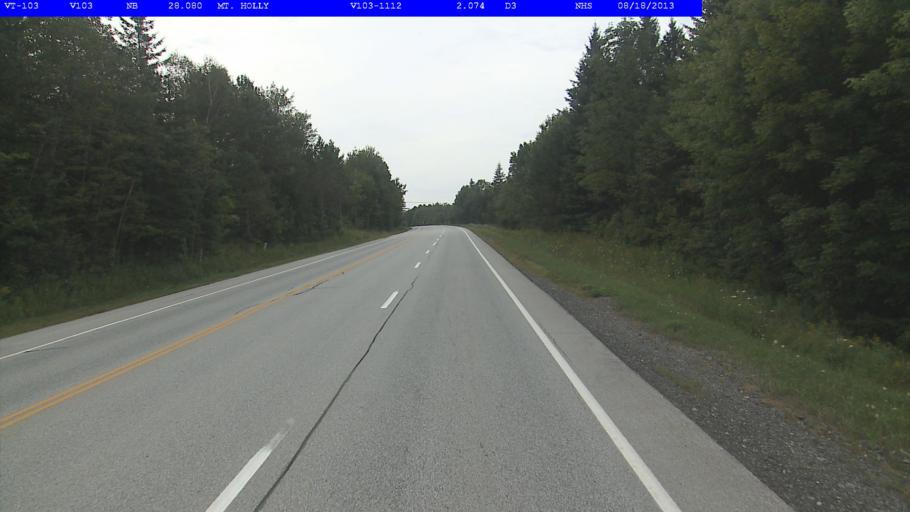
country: US
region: Vermont
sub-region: Windsor County
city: Chester
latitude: 43.4444
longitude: -72.7703
